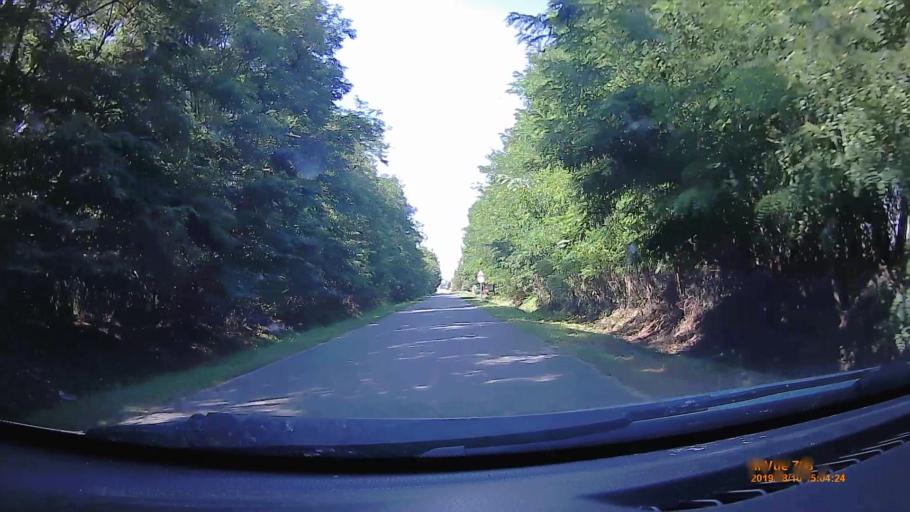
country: HU
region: Somogy
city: Lengyeltoti
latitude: 46.6749
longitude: 17.5666
